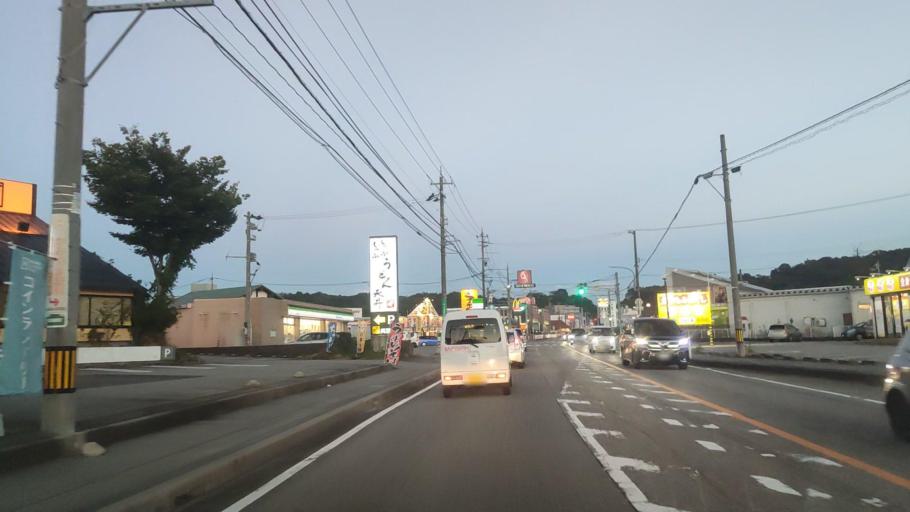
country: JP
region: Toyama
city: Kuragaki-kosugi
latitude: 36.7094
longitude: 137.1735
